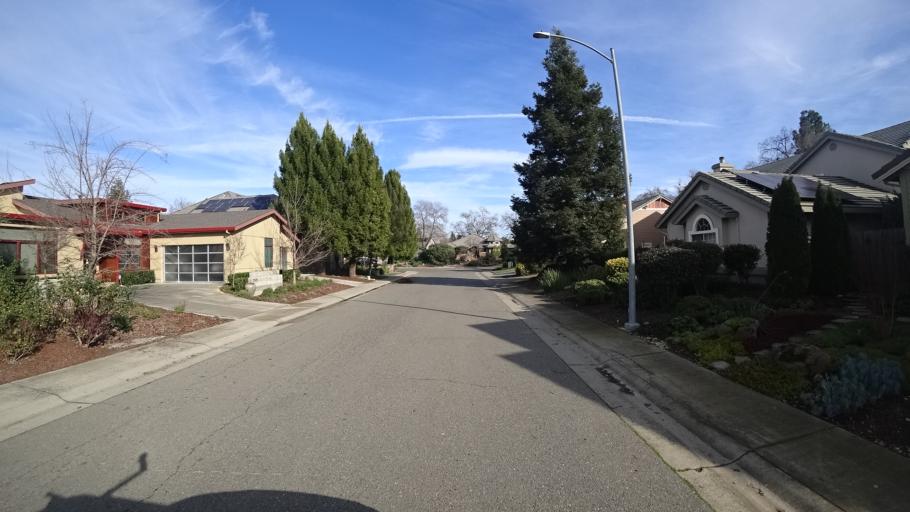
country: US
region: California
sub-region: Yolo County
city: Davis
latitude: 38.5438
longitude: -121.7038
